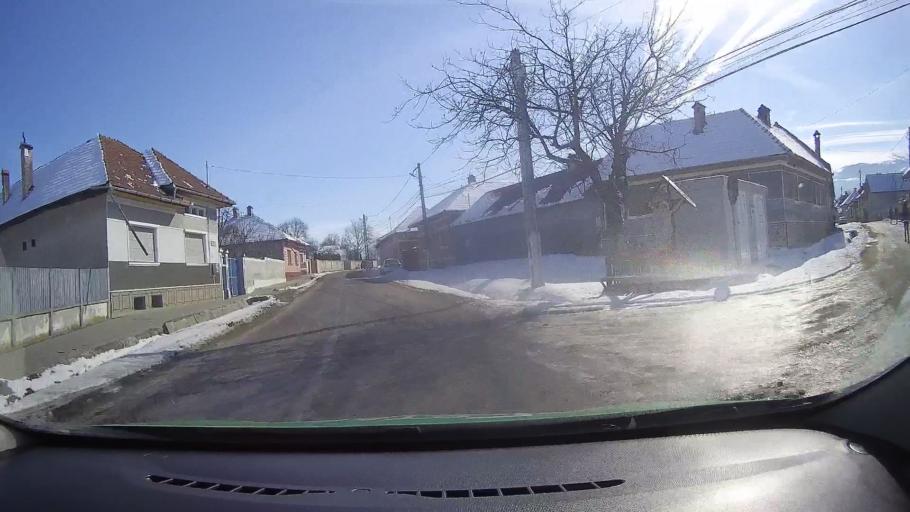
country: RO
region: Brasov
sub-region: Comuna Lisa
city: Lisa
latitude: 45.7249
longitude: 24.8520
